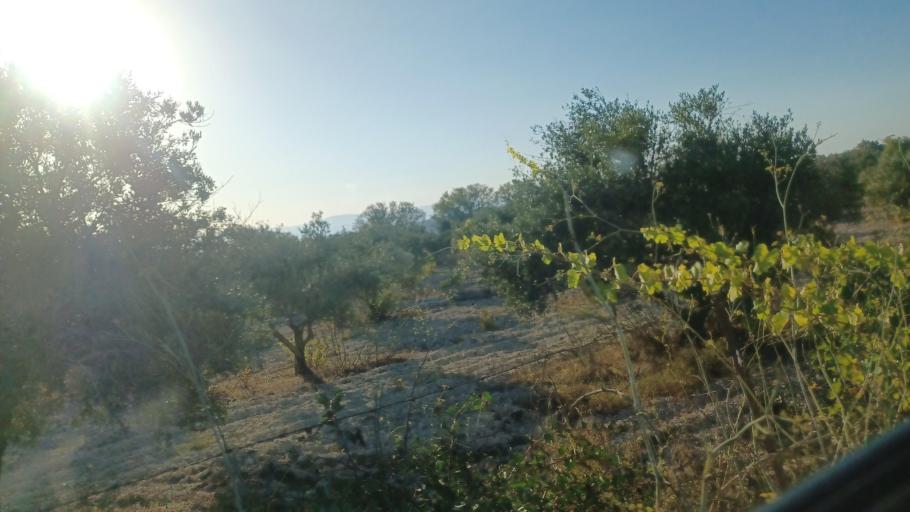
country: CY
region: Pafos
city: Tala
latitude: 34.8569
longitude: 32.4716
